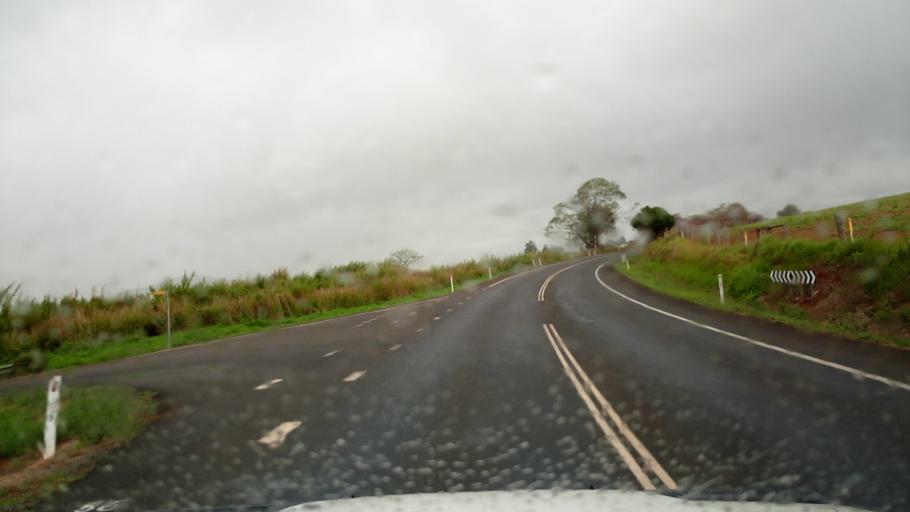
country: AU
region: Queensland
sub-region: Tablelands
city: Atherton
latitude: -17.2814
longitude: 145.6059
